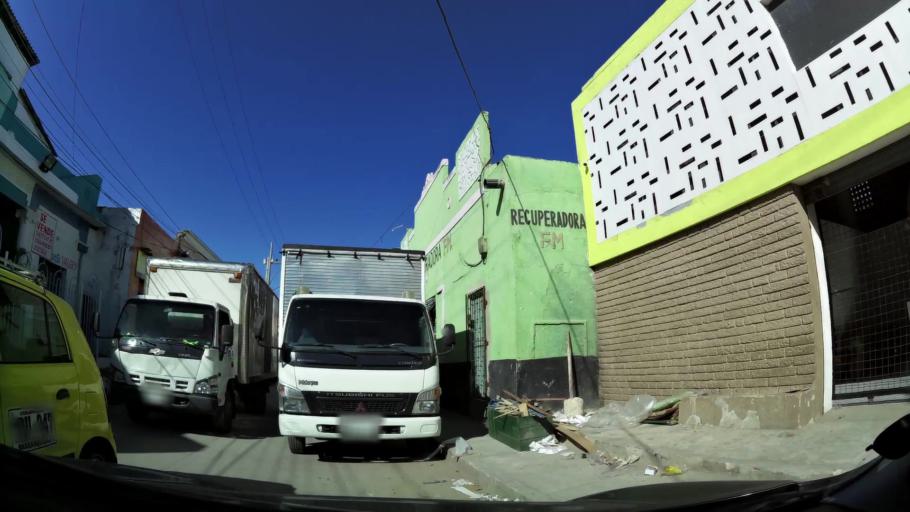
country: CO
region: Atlantico
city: Barranquilla
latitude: 10.9775
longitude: -74.7786
